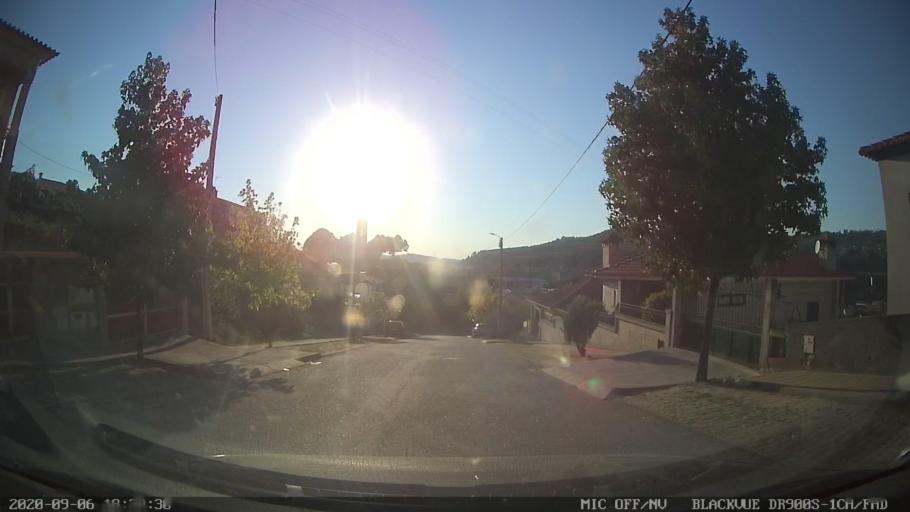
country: PT
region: Porto
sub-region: Amarante
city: Amarante
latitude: 41.2538
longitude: -8.0266
